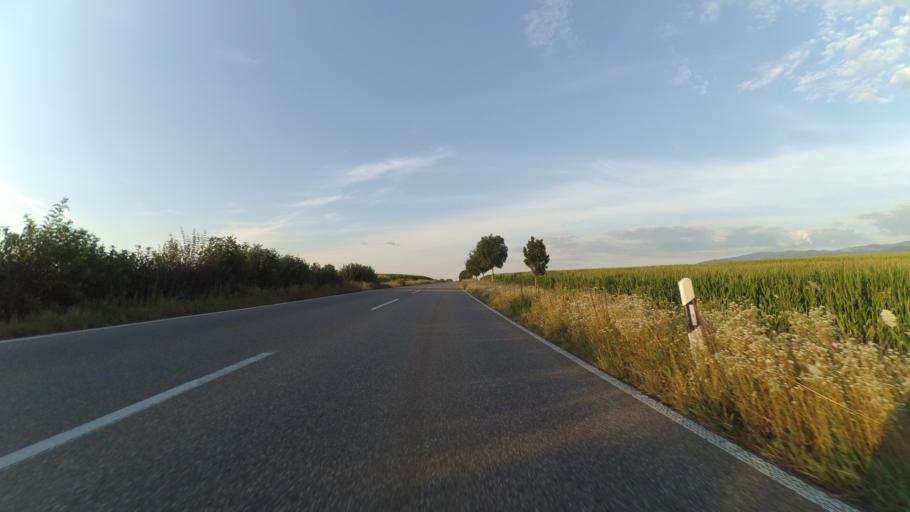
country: DE
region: Baden-Wuerttemberg
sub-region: Freiburg Region
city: Unterkrozingen
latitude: 47.9063
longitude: 7.6876
